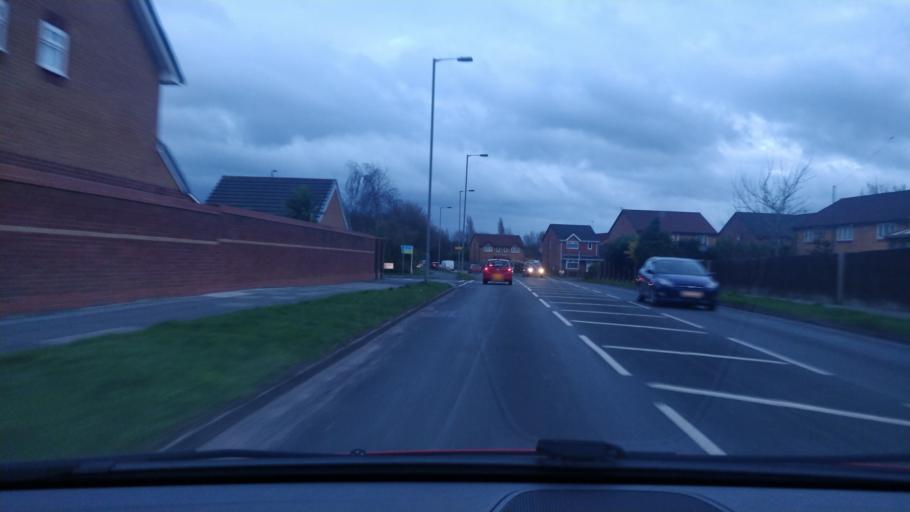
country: GB
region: England
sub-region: Knowsley
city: Kirkby
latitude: 53.4478
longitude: -2.9011
